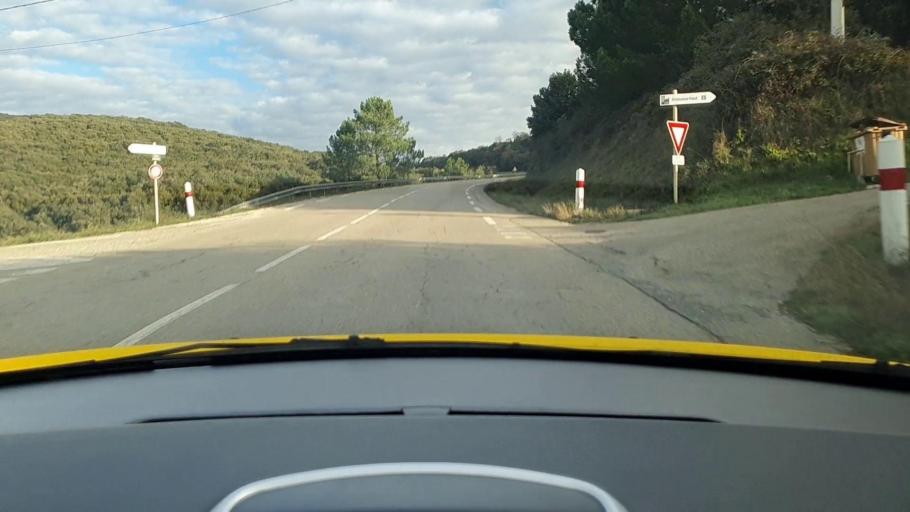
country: FR
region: Languedoc-Roussillon
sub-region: Departement du Gard
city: Laval-Pradel
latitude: 44.2031
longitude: 4.0921
